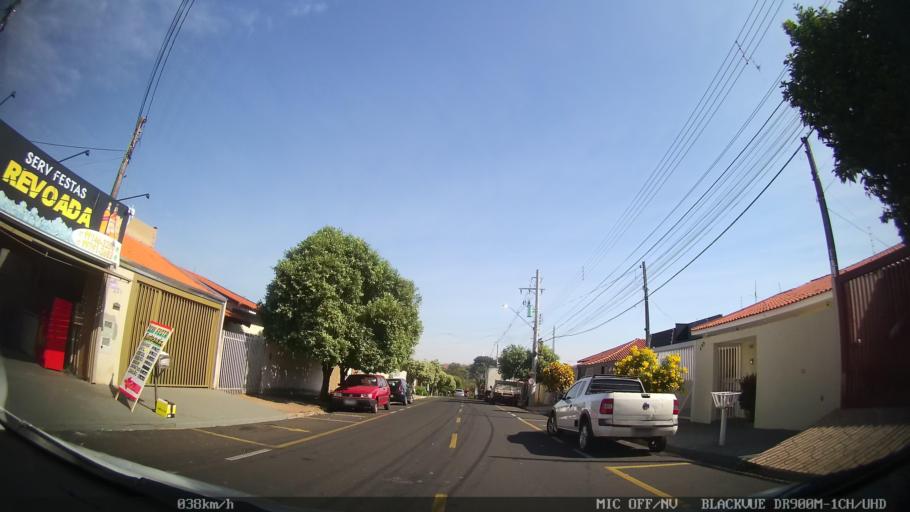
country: BR
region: Sao Paulo
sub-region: Sao Jose Do Rio Preto
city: Sao Jose do Rio Preto
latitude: -20.7880
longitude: -49.4334
